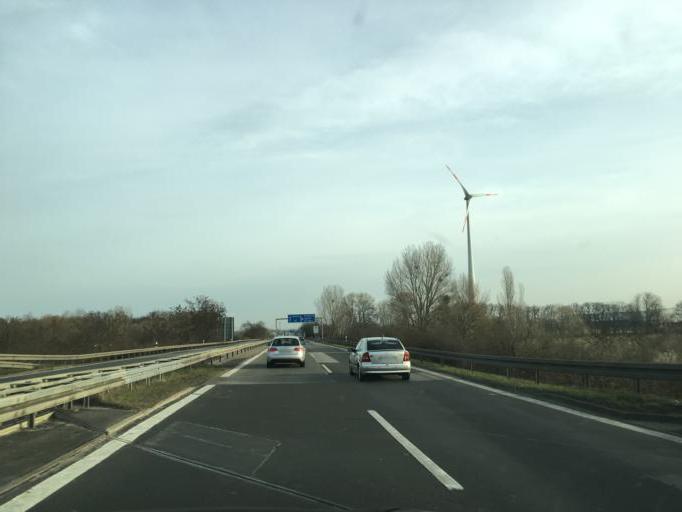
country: DE
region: Berlin
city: Buchholz
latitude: 52.6309
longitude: 13.4274
